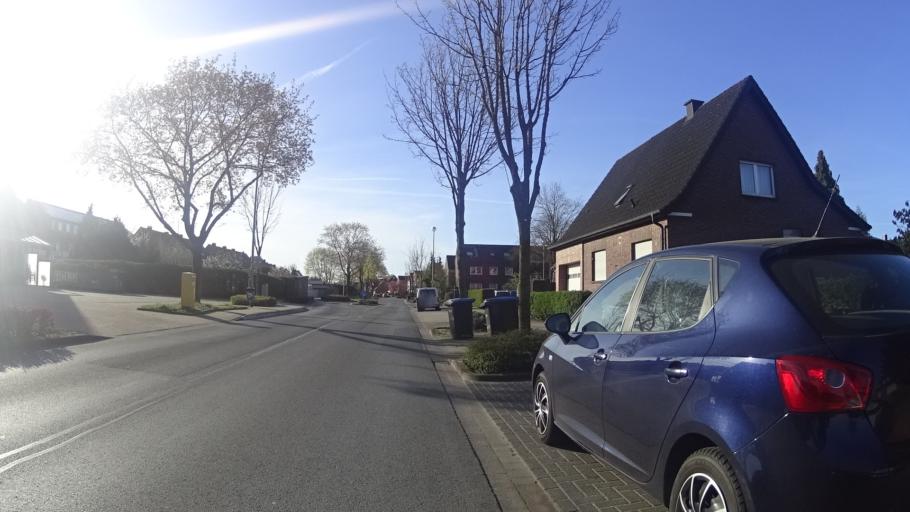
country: DE
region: North Rhine-Westphalia
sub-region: Regierungsbezirk Munster
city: Greven
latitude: 52.0994
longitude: 7.5894
